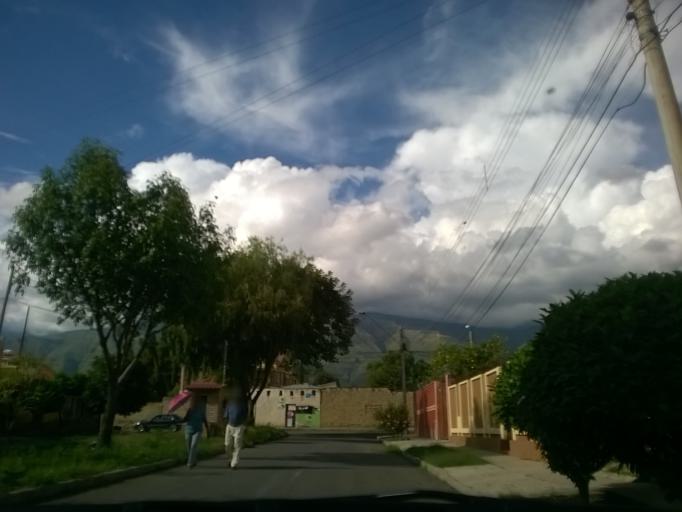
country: BO
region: Cochabamba
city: Cochabamba
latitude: -17.3649
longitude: -66.1846
